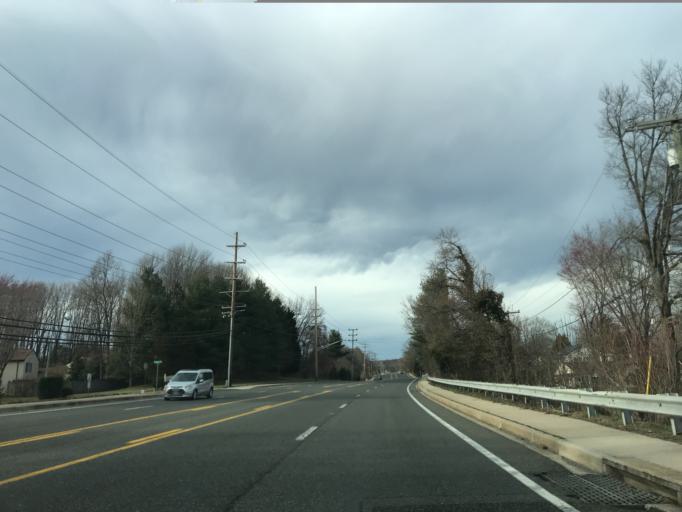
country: US
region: Maryland
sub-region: Prince George's County
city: Bowie
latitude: 38.9888
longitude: -76.7581
